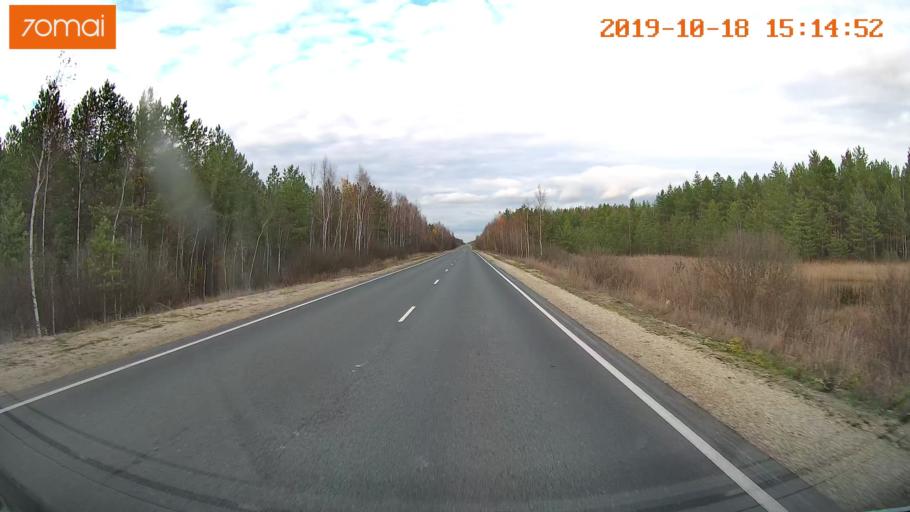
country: RU
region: Vladimir
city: Gus'-Khrustal'nyy
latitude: 55.6096
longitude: 40.7212
